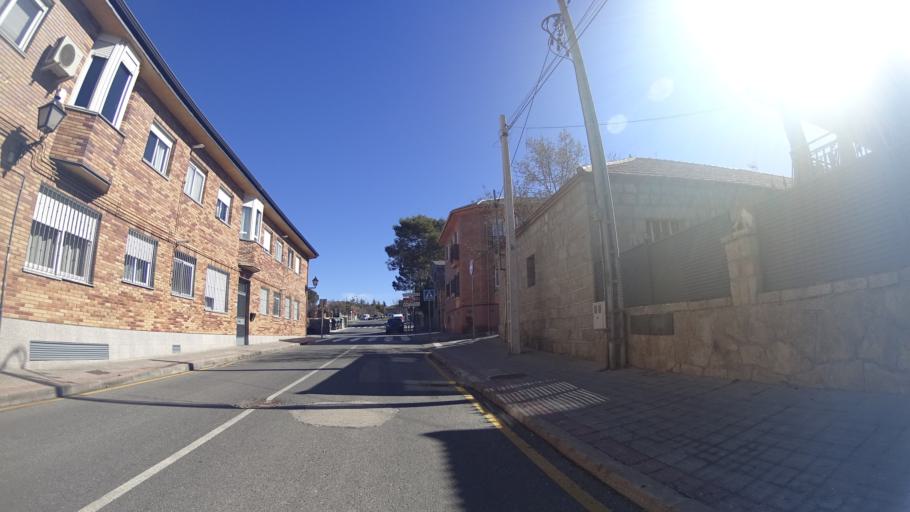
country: ES
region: Madrid
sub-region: Provincia de Madrid
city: Colmenarejo
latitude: 40.5608
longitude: -4.0146
